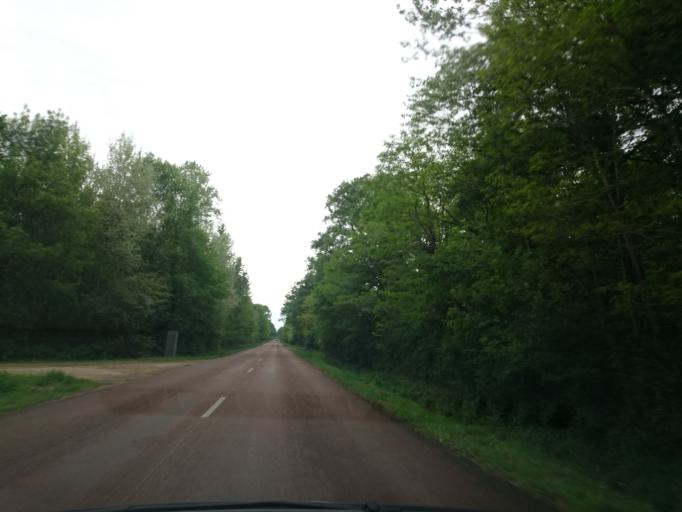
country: FR
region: Centre
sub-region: Departement du Loir-et-Cher
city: Muides-sur-Loire
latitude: 47.6473
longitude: 1.5272
